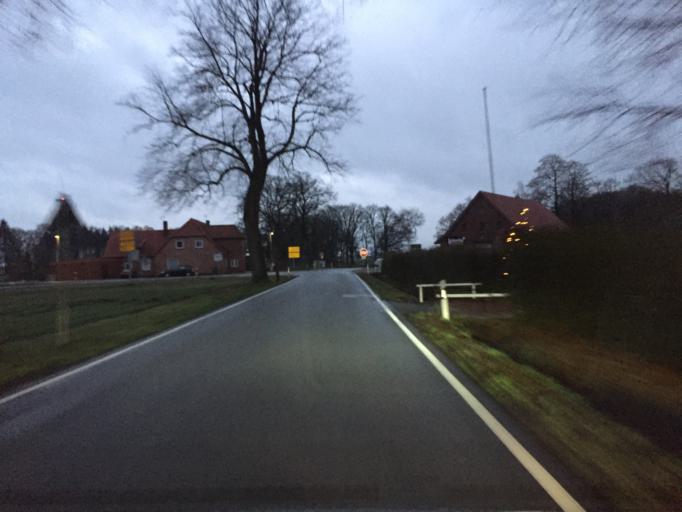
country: DE
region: Lower Saxony
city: Schwaforden
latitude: 52.7507
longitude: 8.8322
